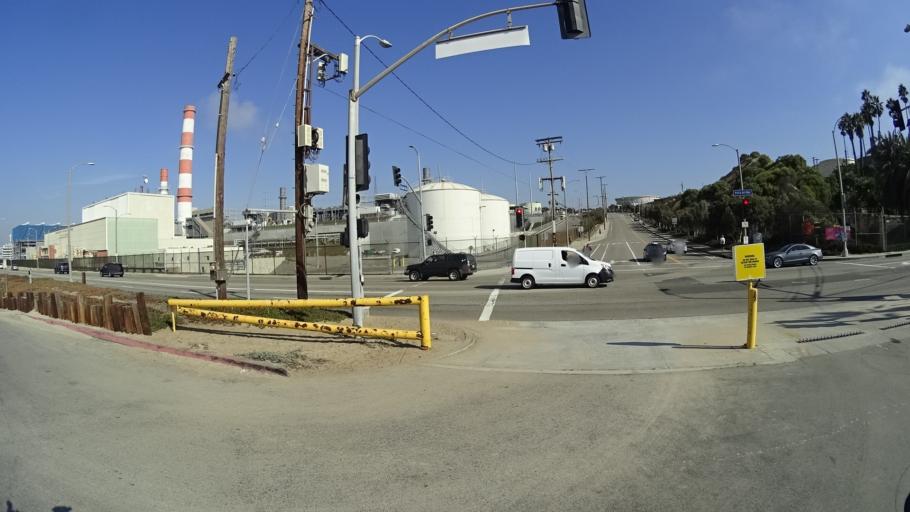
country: US
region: California
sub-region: Los Angeles County
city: El Segundo
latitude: 33.9164
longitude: -118.4280
